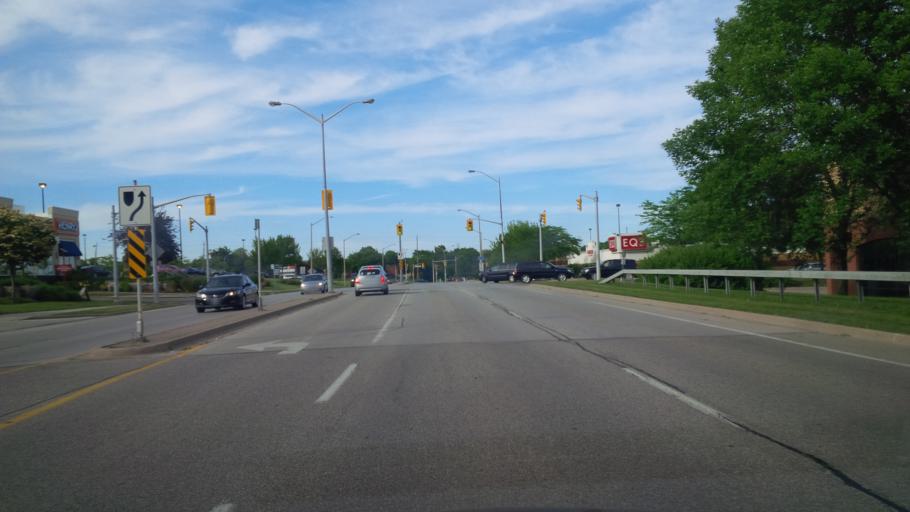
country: CA
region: Ontario
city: Burlington
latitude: 43.3422
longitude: -79.8274
